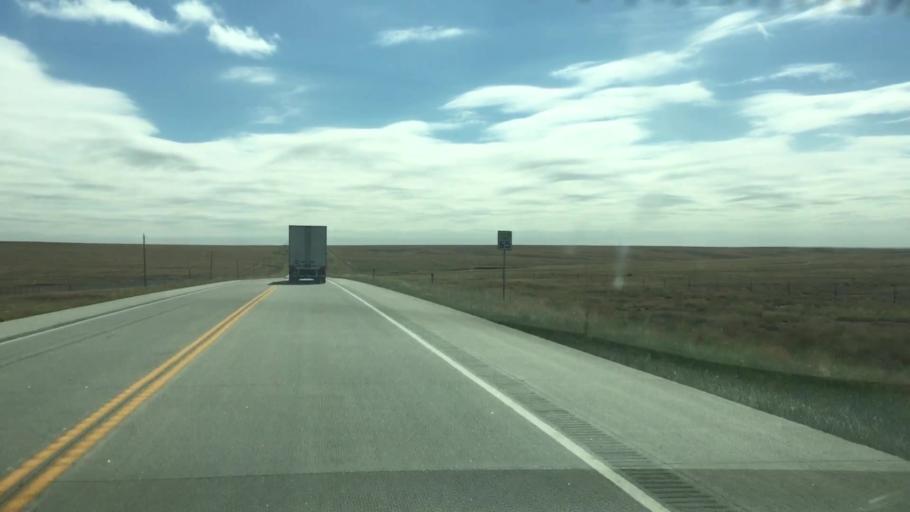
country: US
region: Colorado
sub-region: Lincoln County
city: Hugo
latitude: 39.0176
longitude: -103.3076
